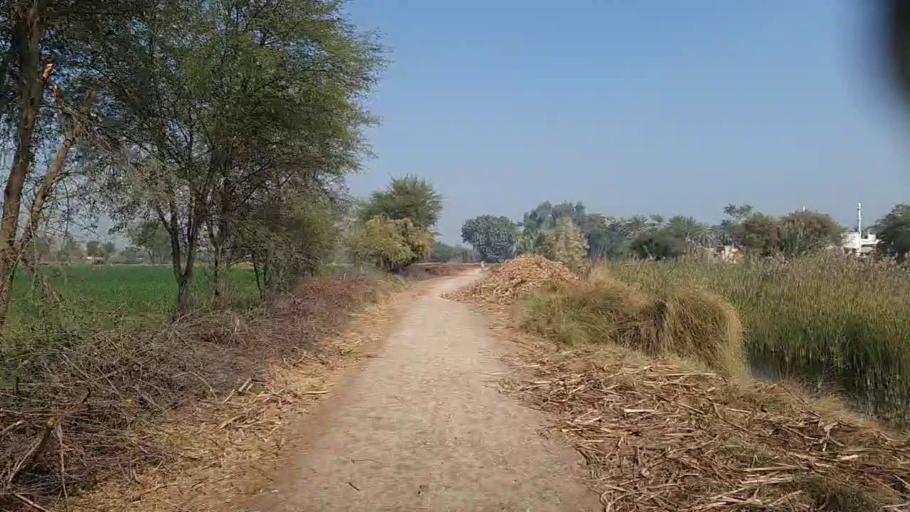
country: PK
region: Sindh
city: Khairpur
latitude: 27.9334
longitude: 69.6705
